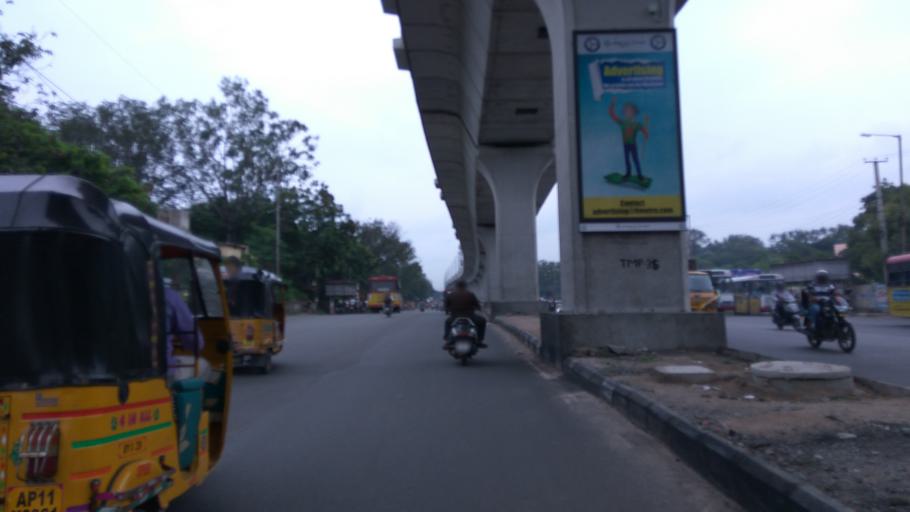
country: IN
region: Telangana
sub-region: Hyderabad
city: Malkajgiri
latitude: 17.4347
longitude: 78.5206
